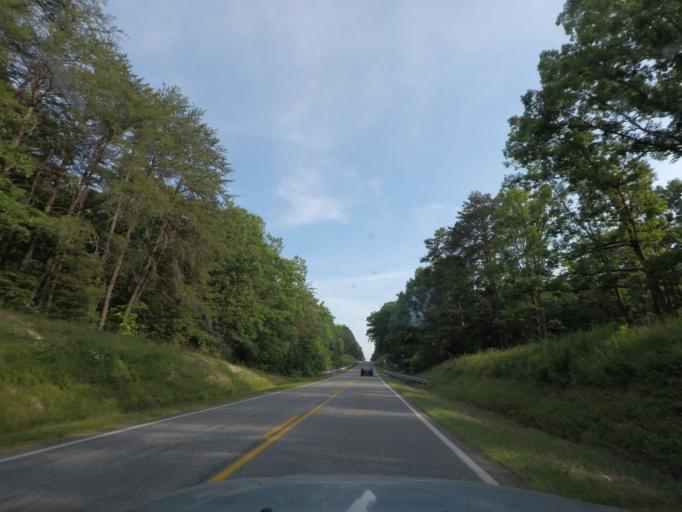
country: US
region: Virginia
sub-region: Mecklenburg County
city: Clarksville
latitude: 36.5866
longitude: -78.5483
